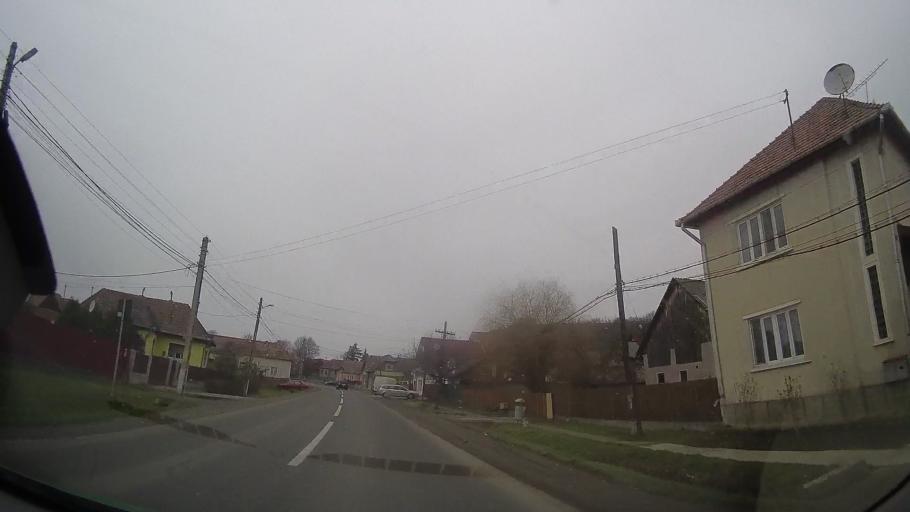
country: RO
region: Mures
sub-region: Comuna Ceausu de Campie
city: Ceausu de Campie
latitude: 46.6420
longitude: 24.5130
